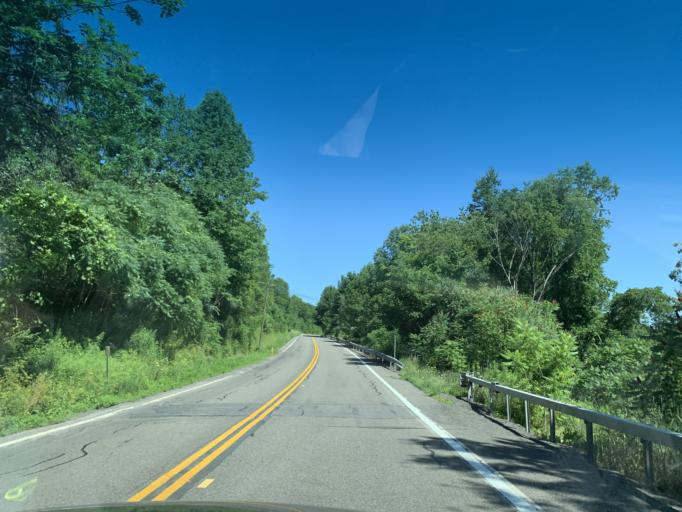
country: US
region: New York
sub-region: Chenango County
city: Norwich
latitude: 42.4752
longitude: -75.4036
